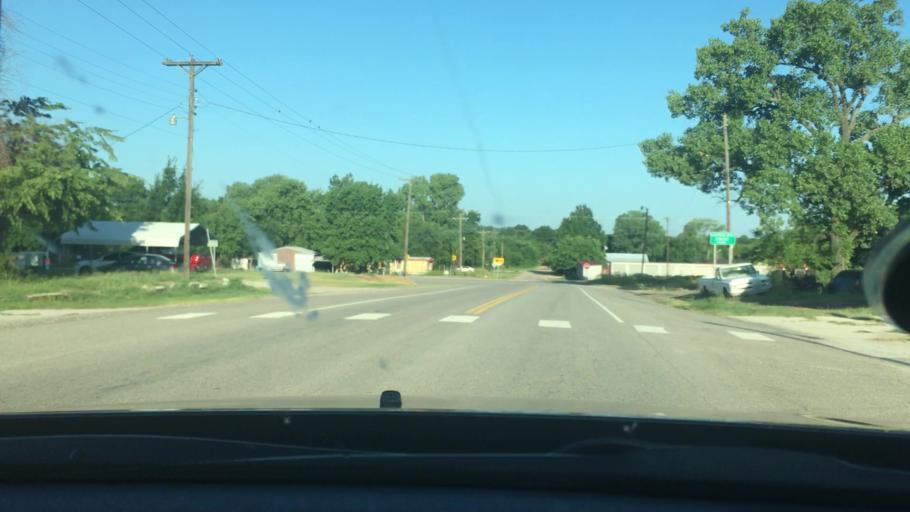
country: US
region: Oklahoma
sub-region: Murray County
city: Sulphur
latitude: 34.6274
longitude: -96.8432
